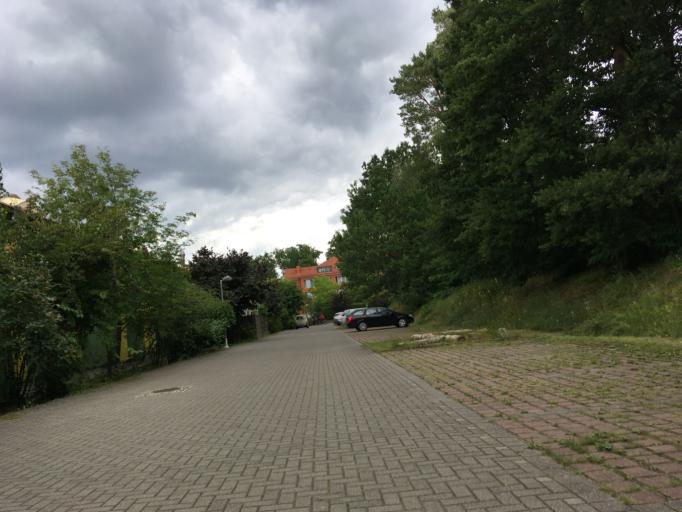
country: DE
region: Brandenburg
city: Wandlitz
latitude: 52.7274
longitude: 13.4910
